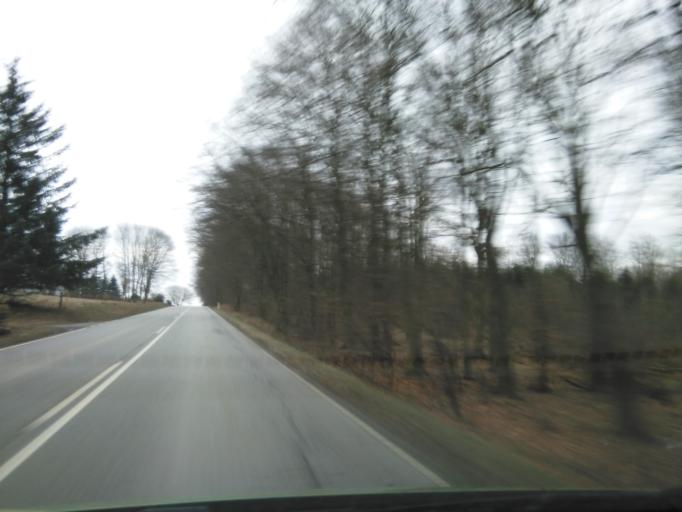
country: DK
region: North Denmark
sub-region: Mariagerfjord Kommune
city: Mariager
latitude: 56.6104
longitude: 9.9922
